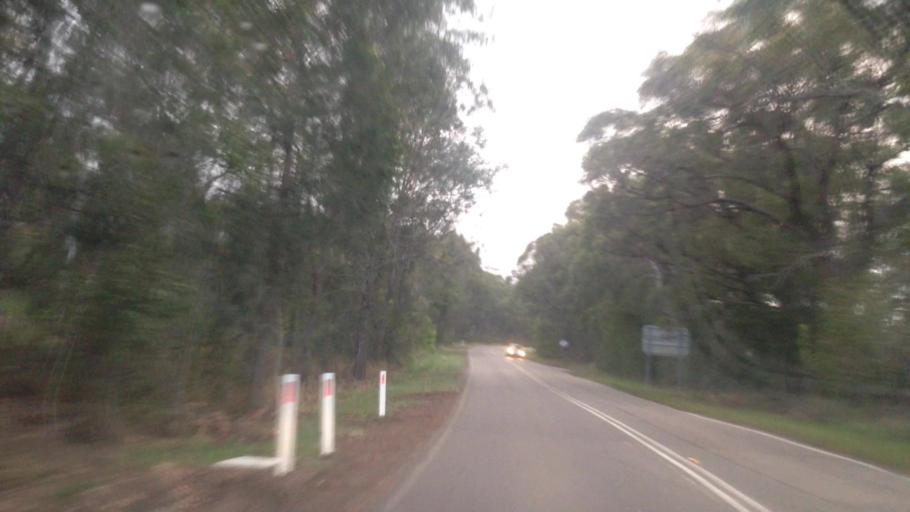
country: AU
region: New South Wales
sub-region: Lake Macquarie Shire
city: Dora Creek
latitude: -33.1087
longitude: 151.4769
